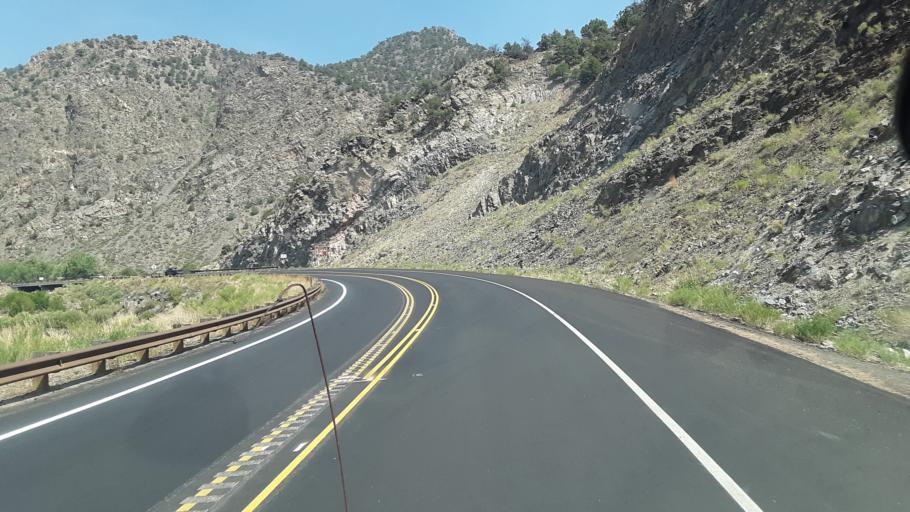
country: US
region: Colorado
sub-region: Fremont County
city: Canon City
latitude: 38.4535
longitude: -105.4964
